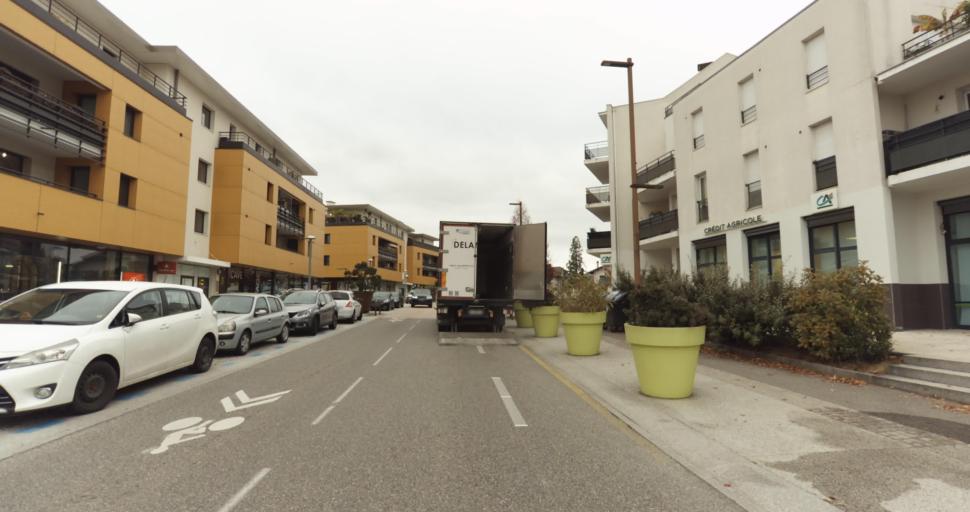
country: FR
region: Rhone-Alpes
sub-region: Departement de la Haute-Savoie
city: Pringy
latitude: 45.9373
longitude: 6.1223
